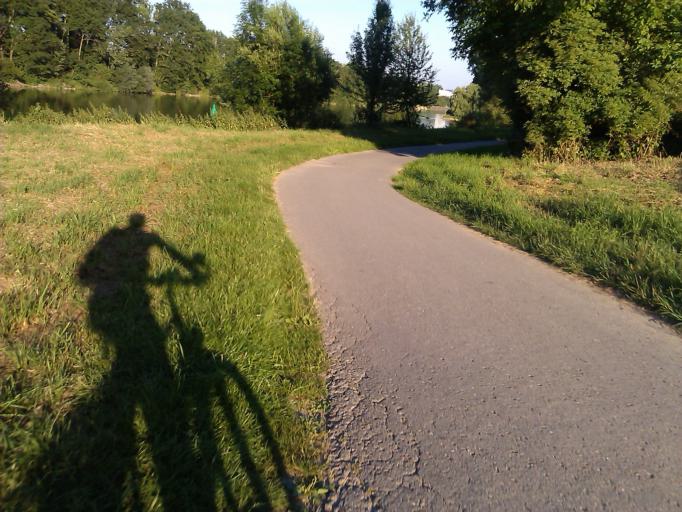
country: DE
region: Baden-Wuerttemberg
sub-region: Regierungsbezirk Stuttgart
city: Untereisesheim
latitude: 49.2256
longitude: 9.1966
